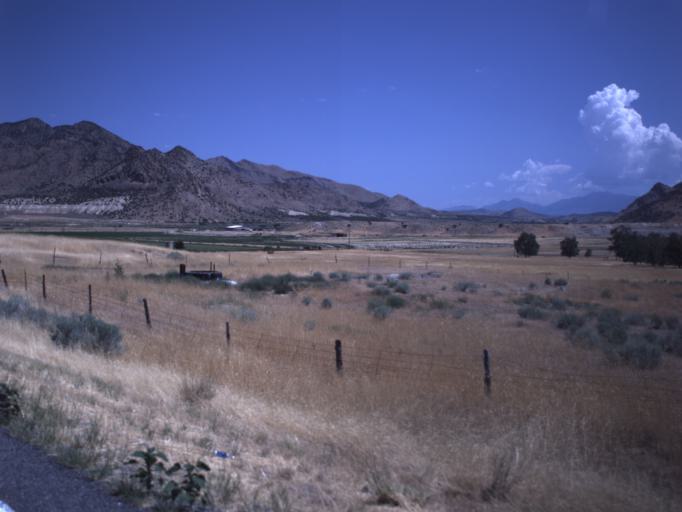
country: US
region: Utah
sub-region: Millard County
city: Delta
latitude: 39.5190
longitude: -112.2733
